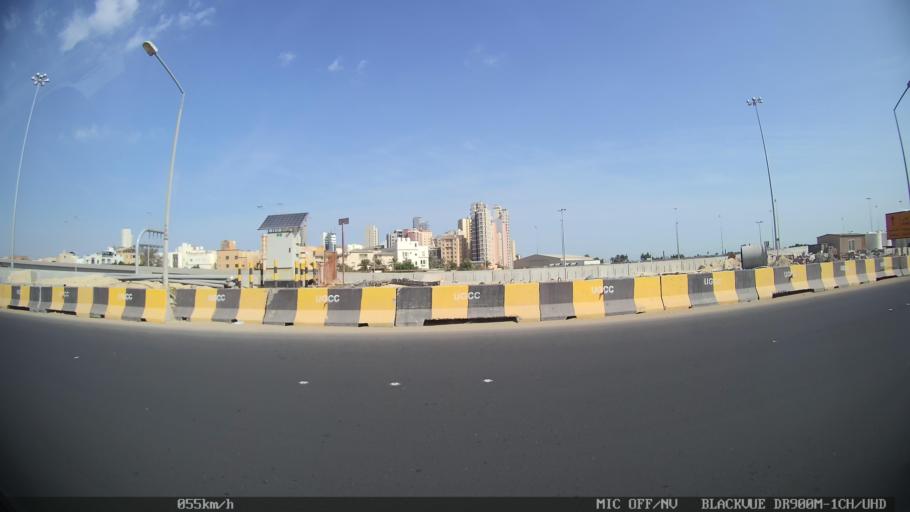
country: KW
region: Muhafazat Hawalli
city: Hawalli
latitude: 29.3440
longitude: 48.0289
